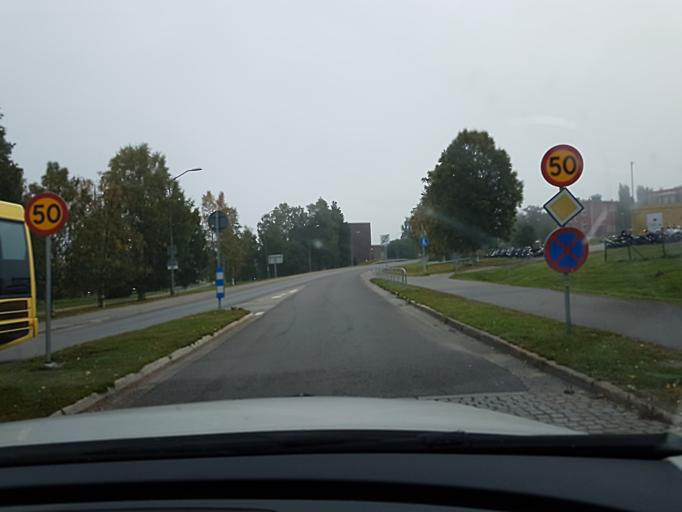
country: SE
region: Norrbotten
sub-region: Pitea Kommun
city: Pitea
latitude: 65.3151
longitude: 21.4924
